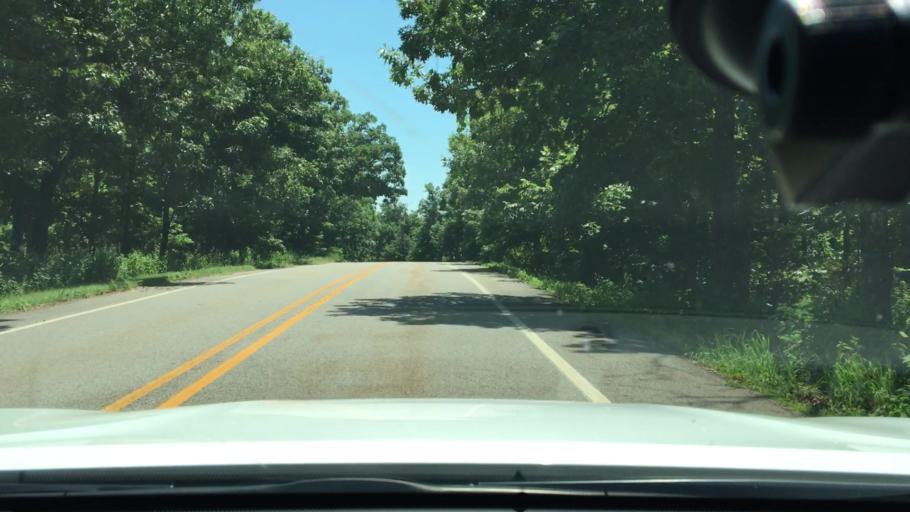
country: US
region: Arkansas
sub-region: Logan County
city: Paris
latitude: 35.1647
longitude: -93.6513
